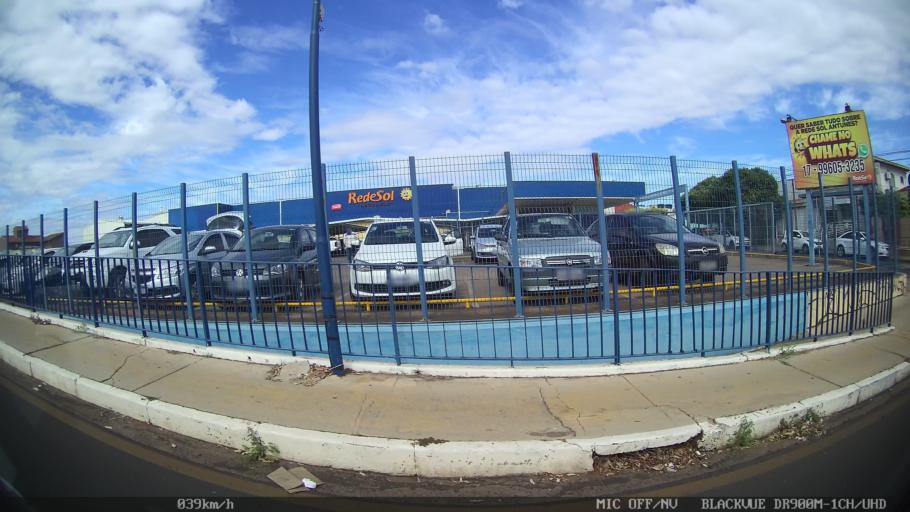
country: BR
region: Sao Paulo
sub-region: Bady Bassitt
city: Bady Bassitt
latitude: -20.8136
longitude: -49.5095
